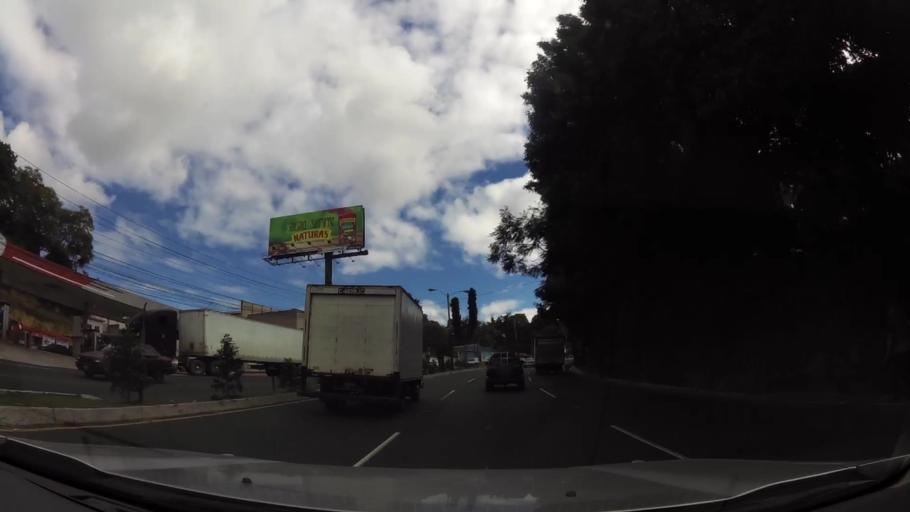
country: GT
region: Guatemala
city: Mixco
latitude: 14.6243
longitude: -90.6052
